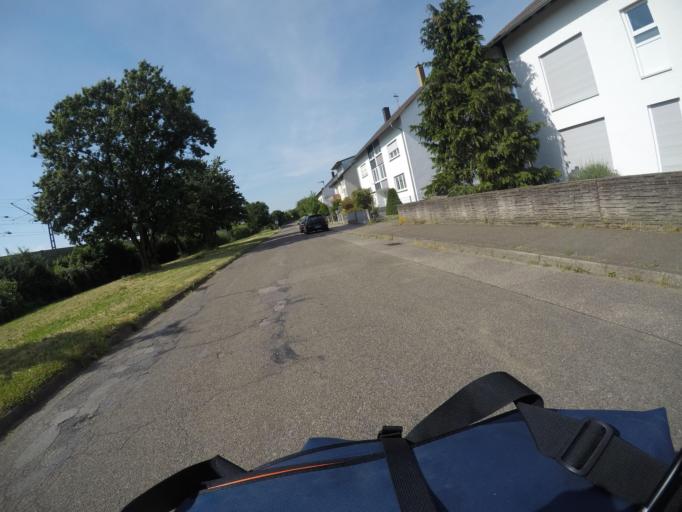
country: DE
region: Baden-Wuerttemberg
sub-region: Karlsruhe Region
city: Bietigheim
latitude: 48.9052
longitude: 8.2534
